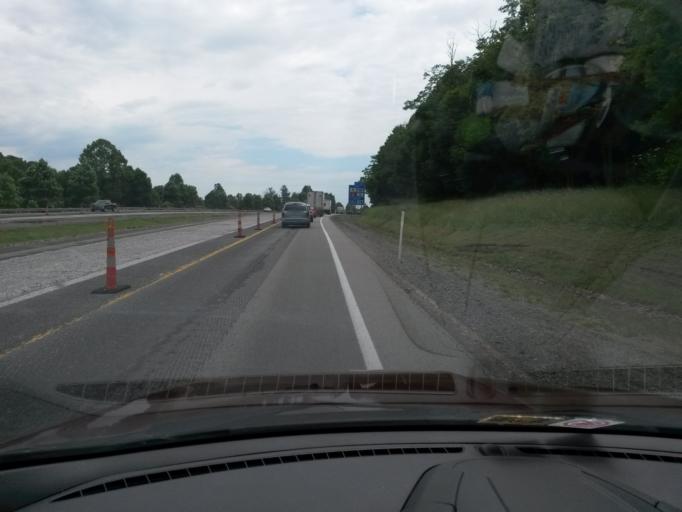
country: US
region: West Virginia
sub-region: Braxton County
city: Sutton
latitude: 38.7234
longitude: -80.6682
